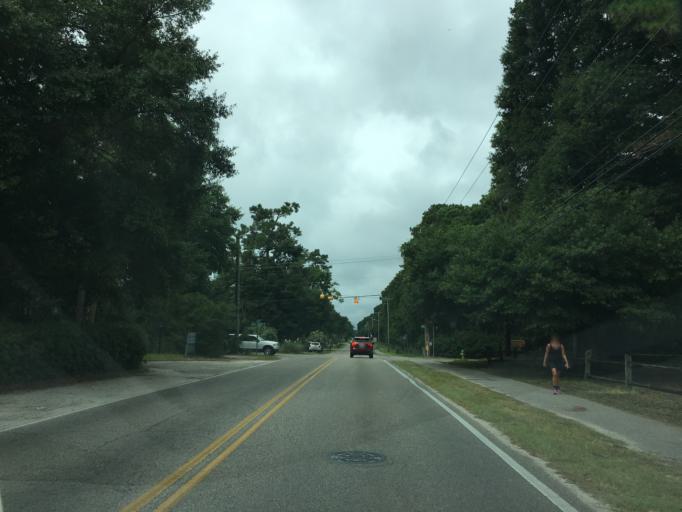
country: US
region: South Carolina
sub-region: Horry County
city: North Myrtle Beach
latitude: 33.7772
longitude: -78.7746
